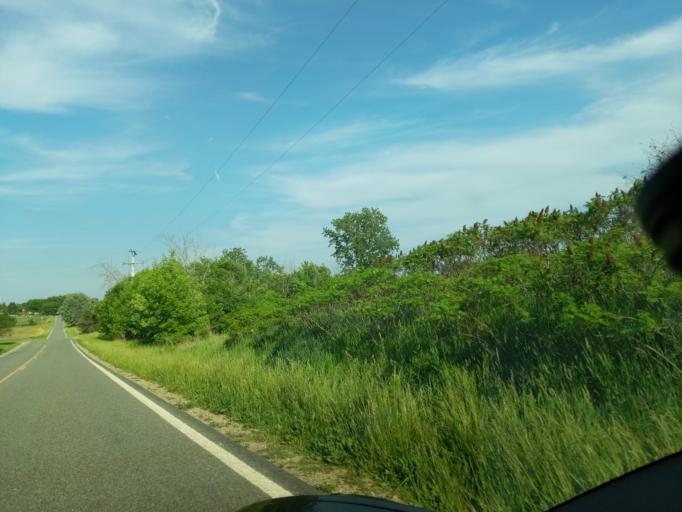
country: US
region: Michigan
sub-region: Barry County
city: Nashville
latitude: 42.6250
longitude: -85.1158
